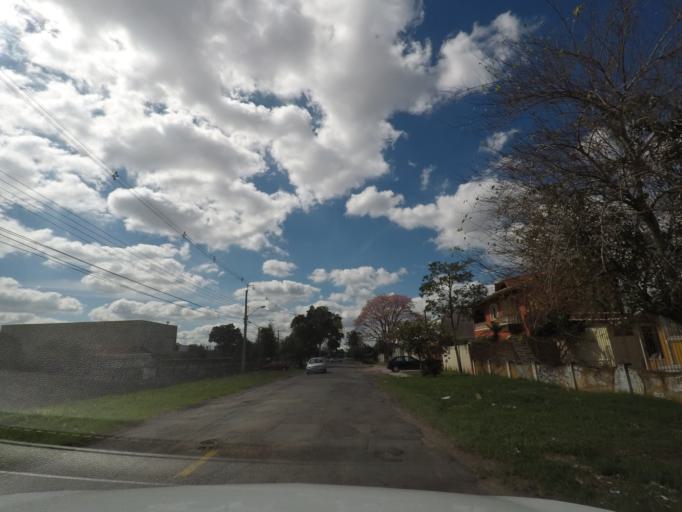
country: BR
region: Parana
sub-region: Sao Jose Dos Pinhais
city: Sao Jose dos Pinhais
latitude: -25.5035
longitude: -49.2325
